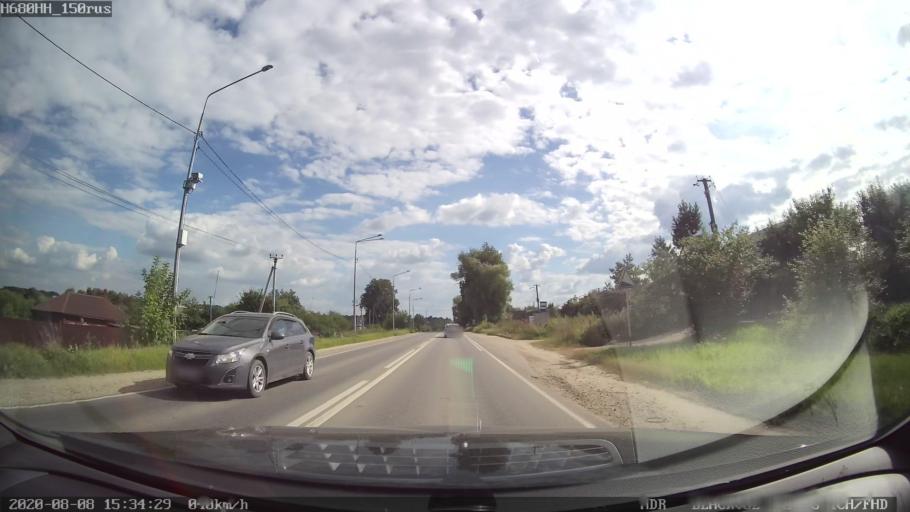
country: RU
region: Tula
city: Zaokskiy
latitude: 54.7613
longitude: 37.4372
